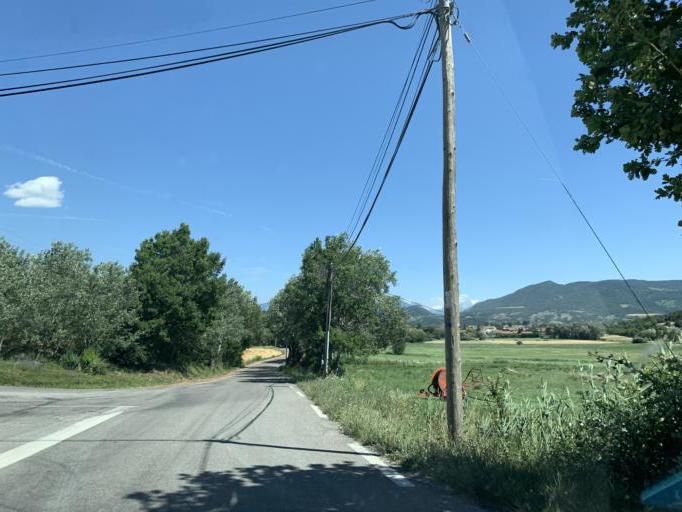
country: FR
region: Provence-Alpes-Cote d'Azur
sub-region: Departement des Hautes-Alpes
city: La Batie-Neuve
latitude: 44.5730
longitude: 6.1845
